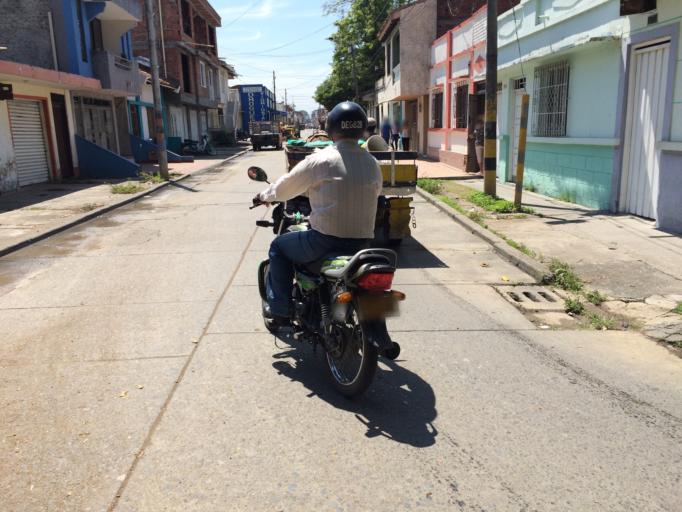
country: CO
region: Valle del Cauca
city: Tulua
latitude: 4.0905
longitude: -76.1977
